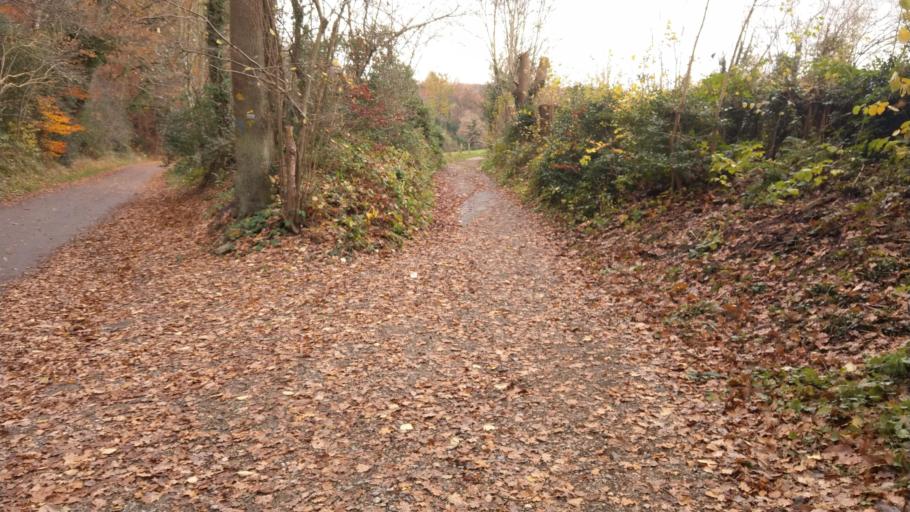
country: DE
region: North Rhine-Westphalia
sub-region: Regierungsbezirk Koln
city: Aachen
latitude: 50.7571
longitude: 6.0547
